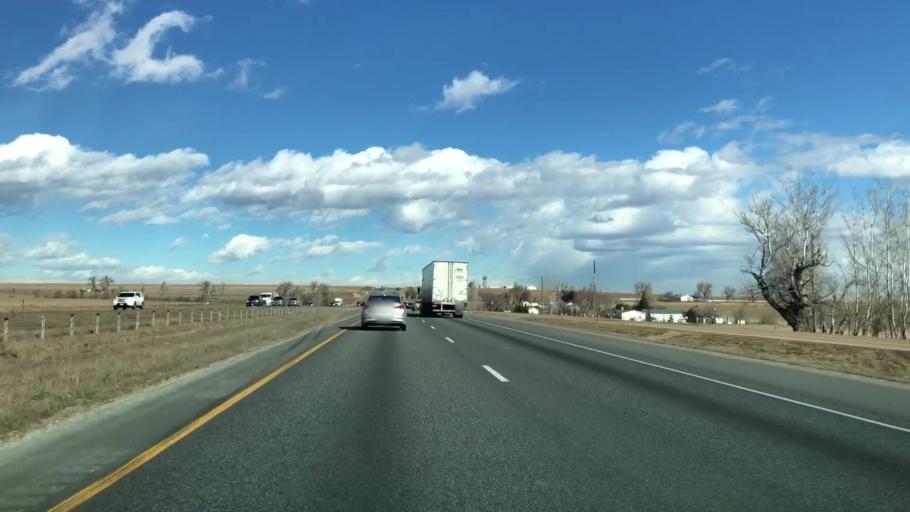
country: US
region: Colorado
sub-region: Weld County
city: Mead
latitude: 40.2537
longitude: -104.9790
